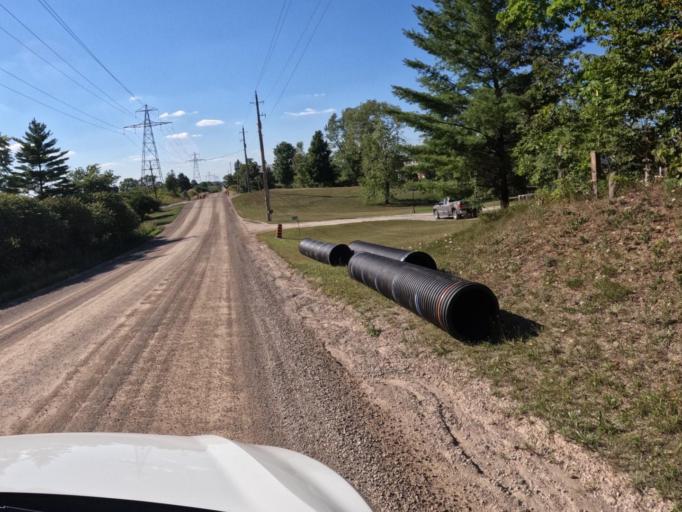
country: CA
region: Ontario
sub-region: Wellington County
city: Guelph
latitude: 43.4372
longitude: -80.1391
